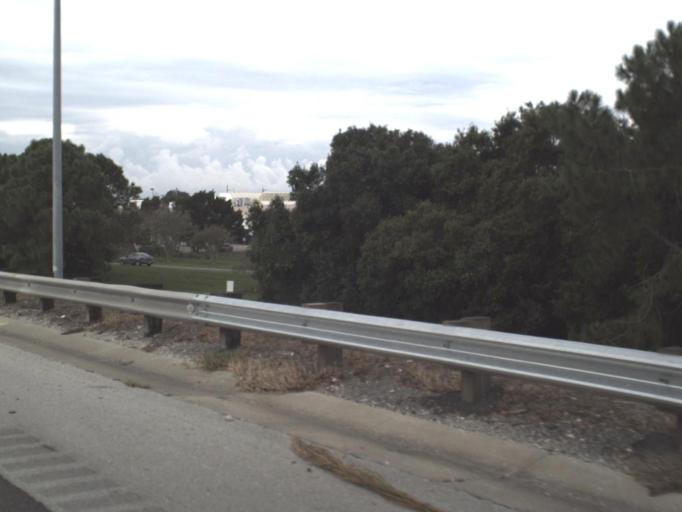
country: US
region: Florida
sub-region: Sarasota County
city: Lake Sarasota
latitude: 27.2974
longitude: -82.4483
